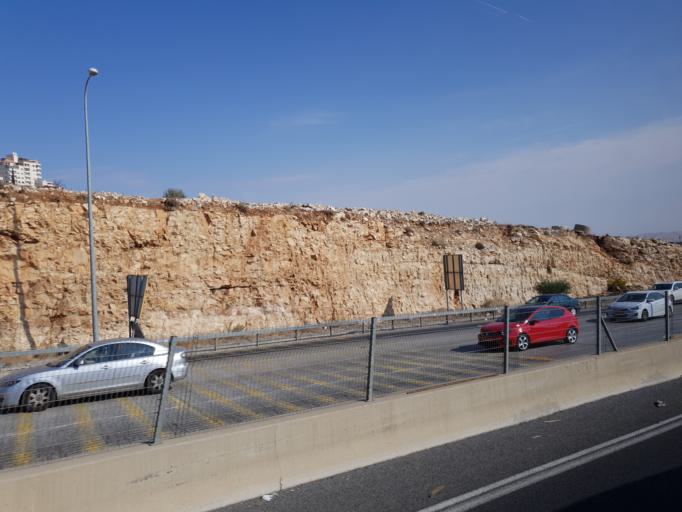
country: PS
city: Az Za`ayyim
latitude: 31.7830
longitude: 35.2645
